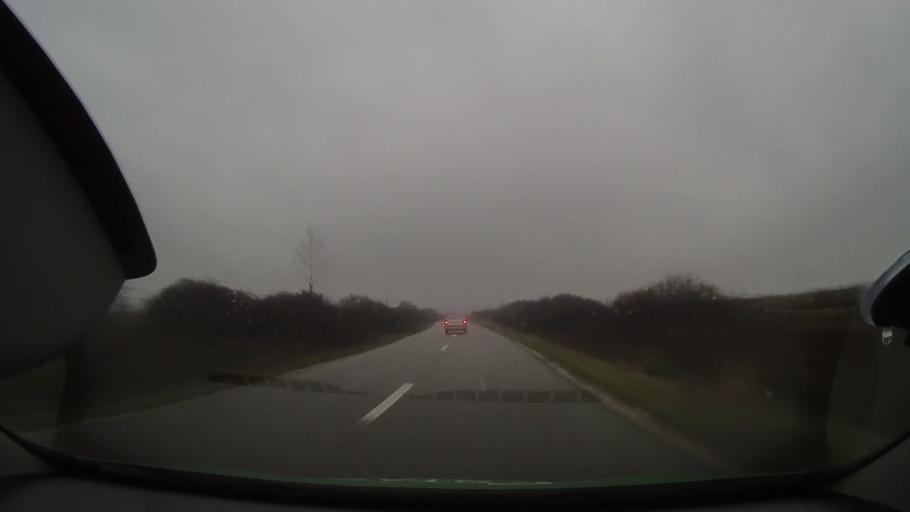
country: RO
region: Arad
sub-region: Comuna Craiova
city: Craiova
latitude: 46.5452
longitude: 21.9597
